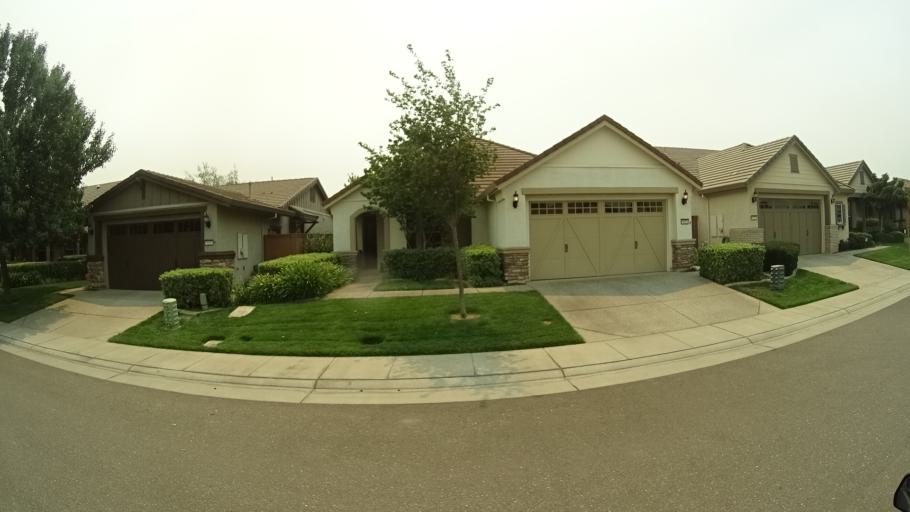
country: US
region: California
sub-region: Sacramento County
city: Laguna
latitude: 38.3952
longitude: -121.4109
